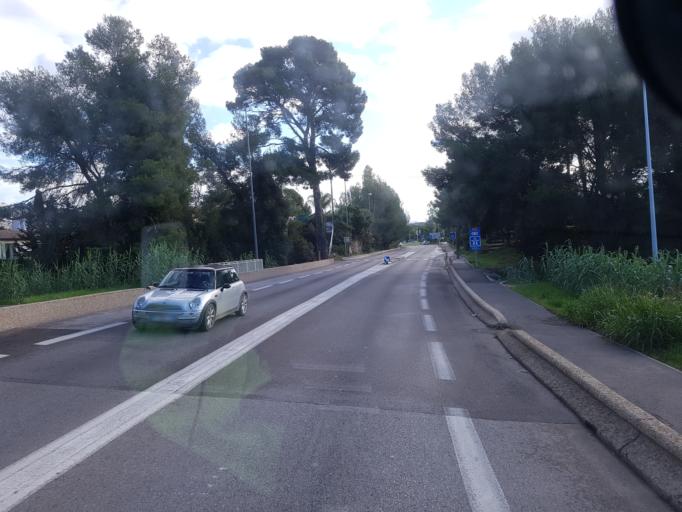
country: FR
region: Provence-Alpes-Cote d'Azur
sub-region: Departement du Var
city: Saint-Cyr-sur-Mer
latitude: 43.1833
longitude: 5.6869
